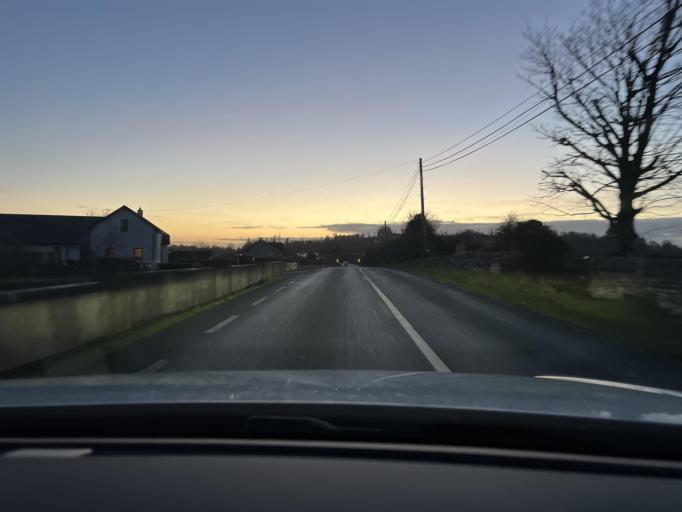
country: IE
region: Connaught
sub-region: County Leitrim
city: Carrick-on-Shannon
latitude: 53.9793
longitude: -8.0545
